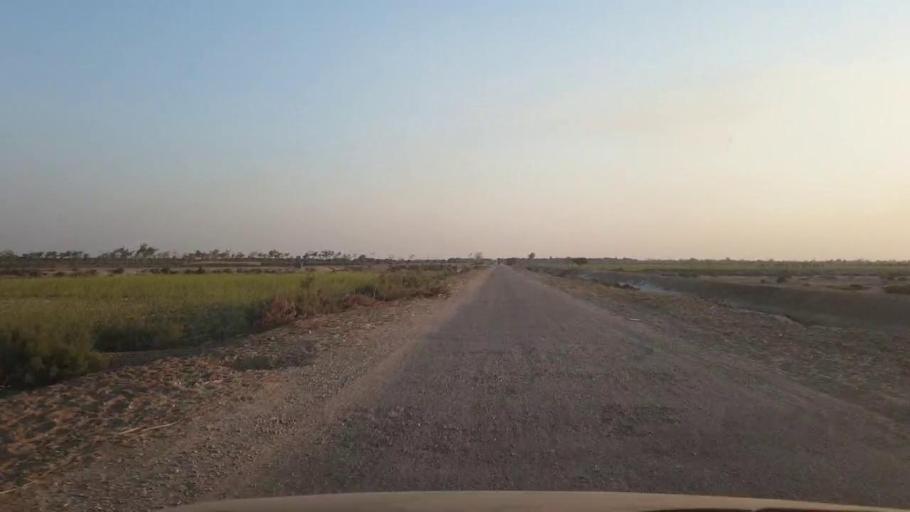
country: PK
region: Sindh
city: Mirwah Gorchani
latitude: 25.2767
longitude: 68.9394
